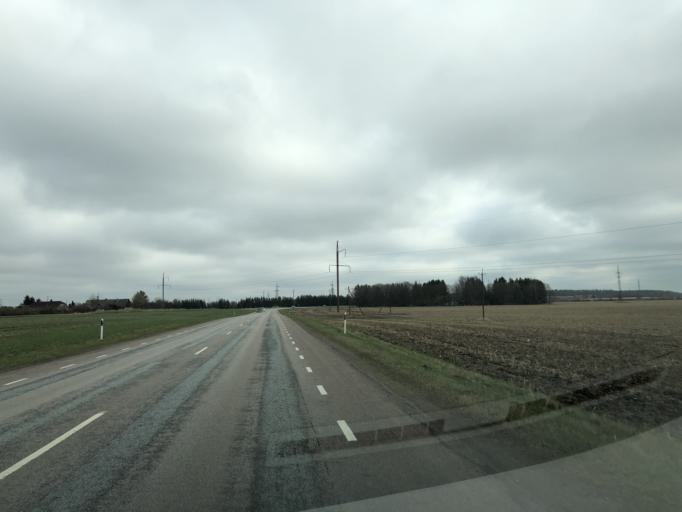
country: EE
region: Laeaene-Virumaa
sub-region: Rakvere linn
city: Rakvere
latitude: 59.3129
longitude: 26.3267
